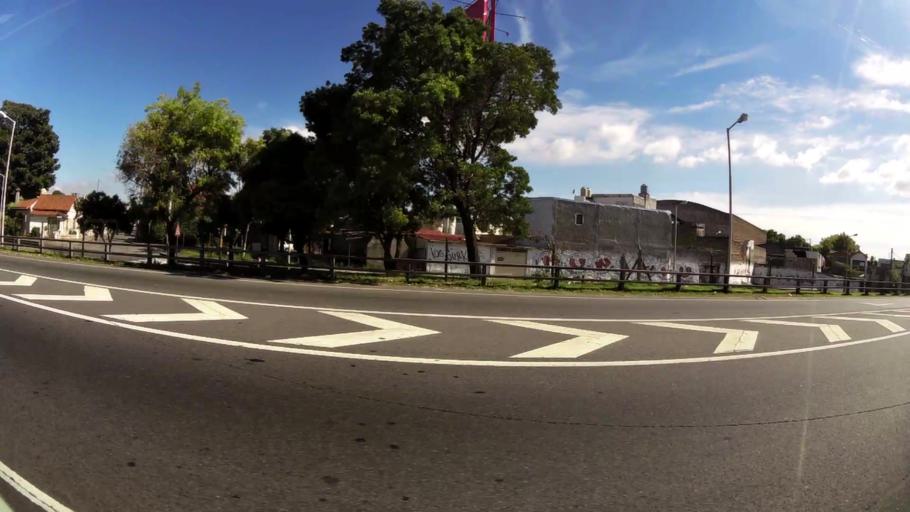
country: AR
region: Buenos Aires
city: Caseros
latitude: -34.6303
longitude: -58.5648
